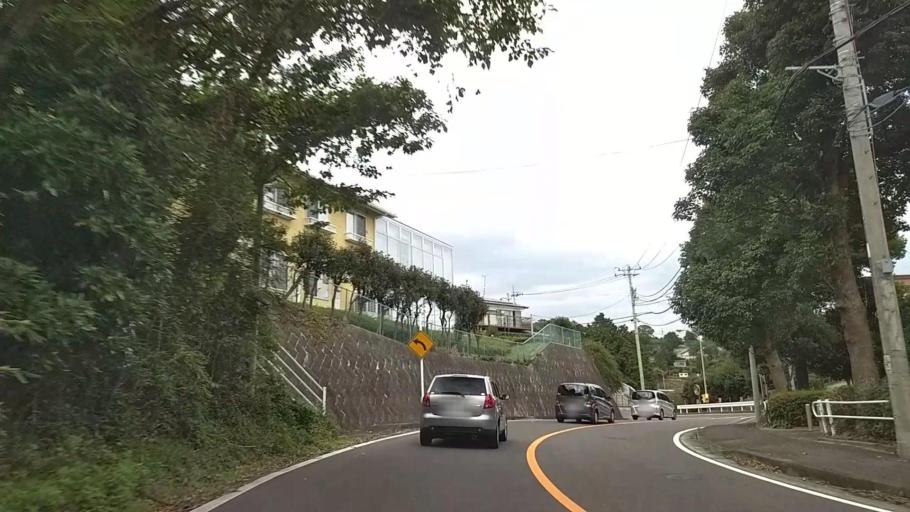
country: JP
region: Kanagawa
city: Yugawara
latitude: 35.1667
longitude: 139.1362
